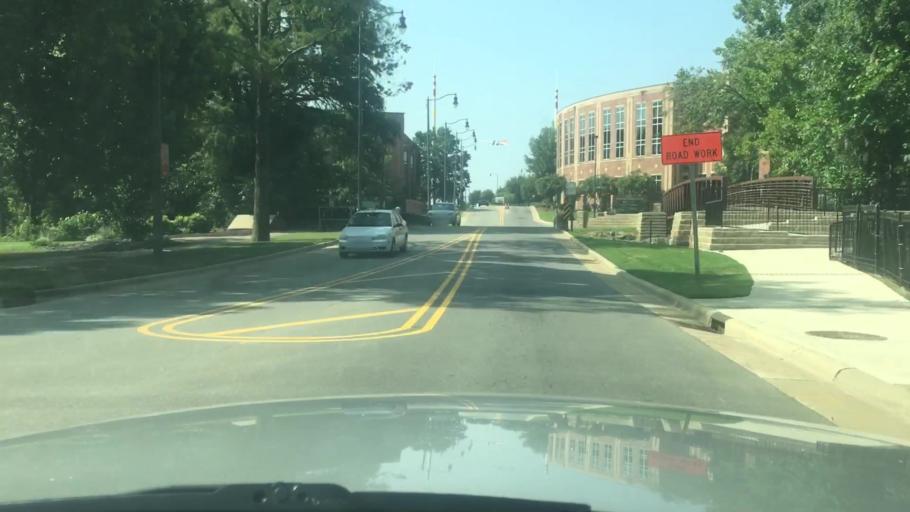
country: US
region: North Carolina
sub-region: Cumberland County
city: Fayetteville
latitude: 35.0568
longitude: -78.8811
